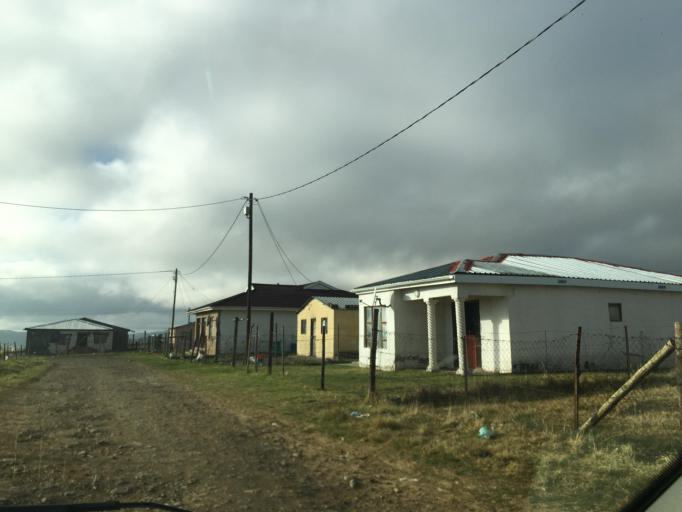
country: ZA
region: Eastern Cape
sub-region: Chris Hani District Municipality
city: Elliot
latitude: -31.3391
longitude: 27.8362
